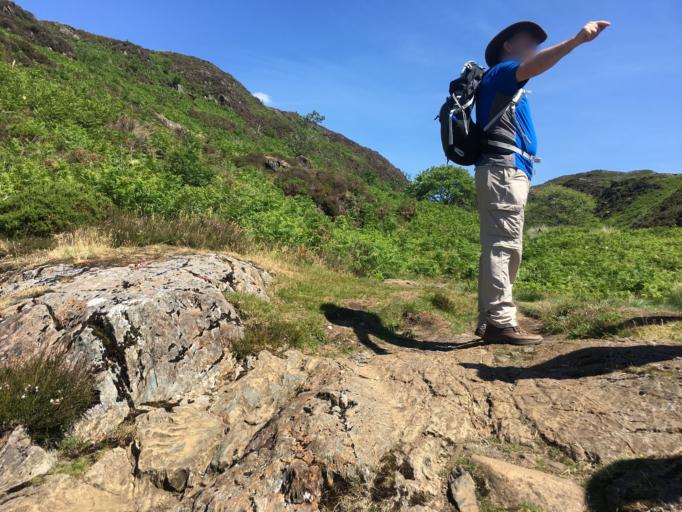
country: GB
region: Wales
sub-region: Gwynedd
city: Penrhyndeudraeth
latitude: 53.0012
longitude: -4.0867
